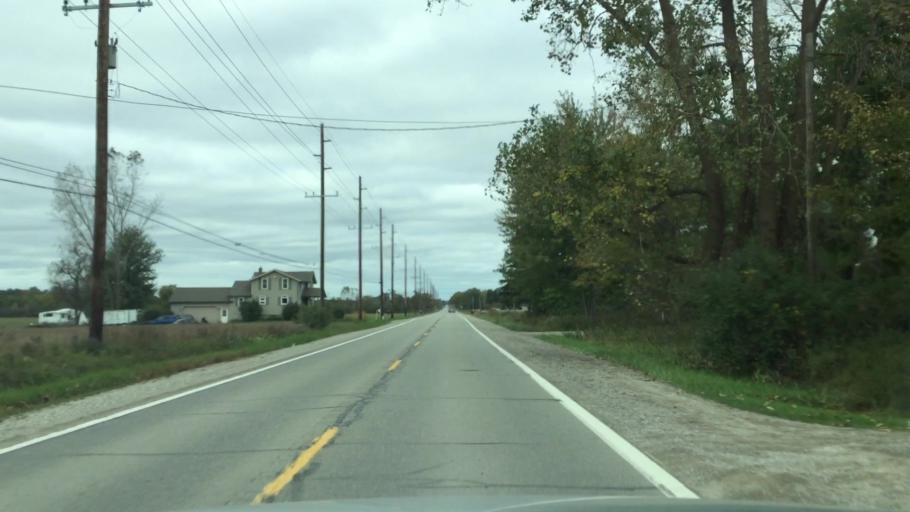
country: US
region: Michigan
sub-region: Macomb County
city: Richmond
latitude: 42.8081
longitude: -82.8081
